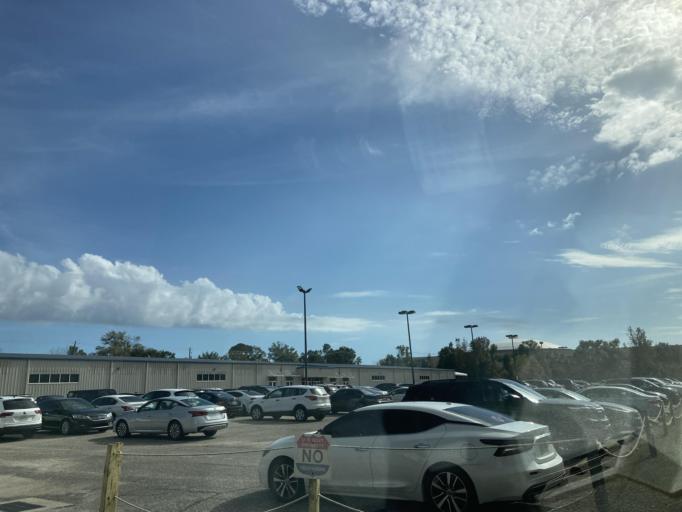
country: US
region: Mississippi
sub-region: Harrison County
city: D'Iberville
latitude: 30.3984
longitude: -88.9761
